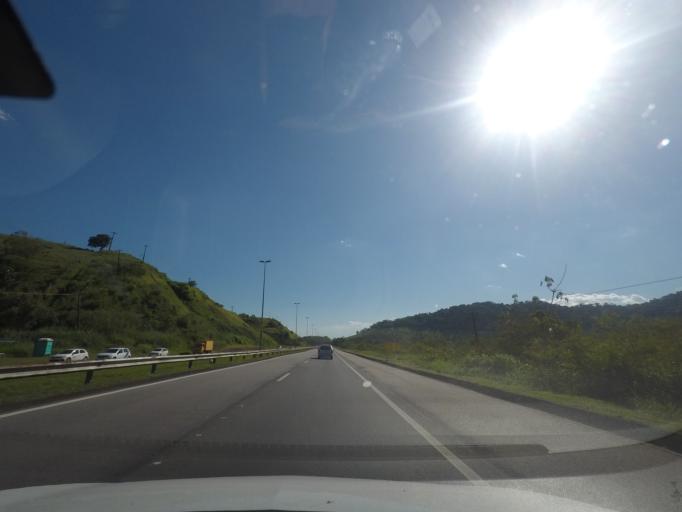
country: BR
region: Rio de Janeiro
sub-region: Guapimirim
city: Guapimirim
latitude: -22.6277
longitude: -43.0483
